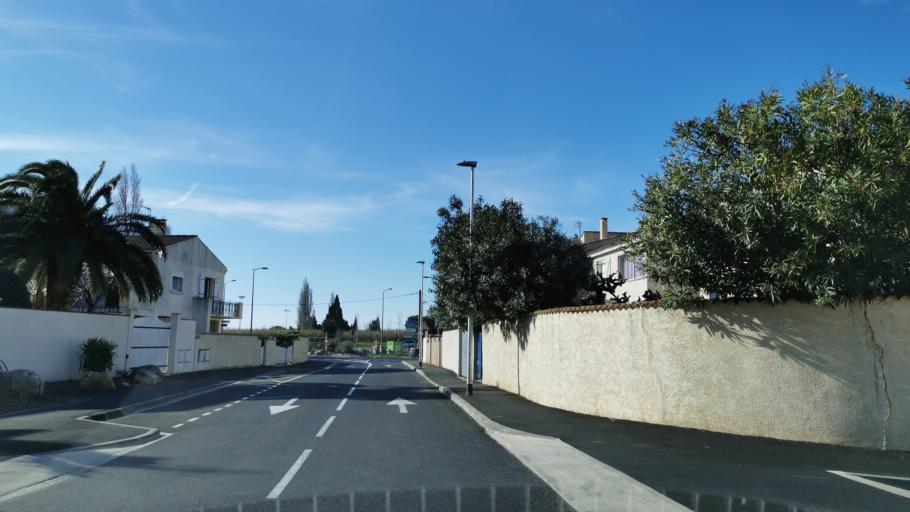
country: FR
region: Languedoc-Roussillon
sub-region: Departement de l'Aude
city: Narbonne
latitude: 43.1763
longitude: 2.9976
